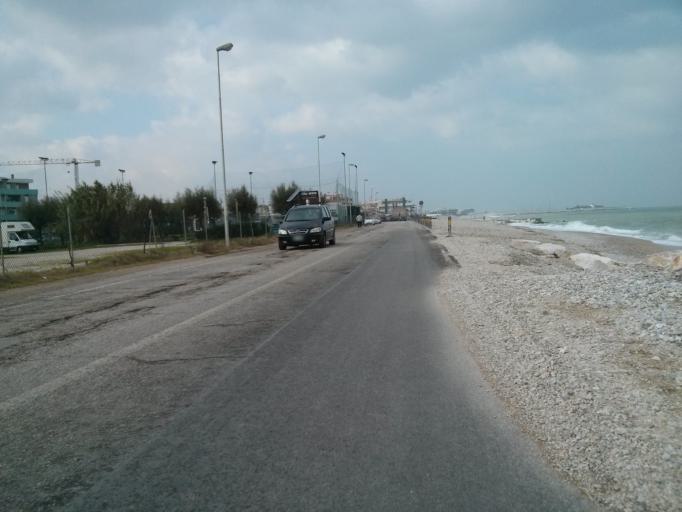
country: IT
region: The Marches
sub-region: Provincia di Pesaro e Urbino
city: Fano
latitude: 43.8426
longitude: 13.0316
